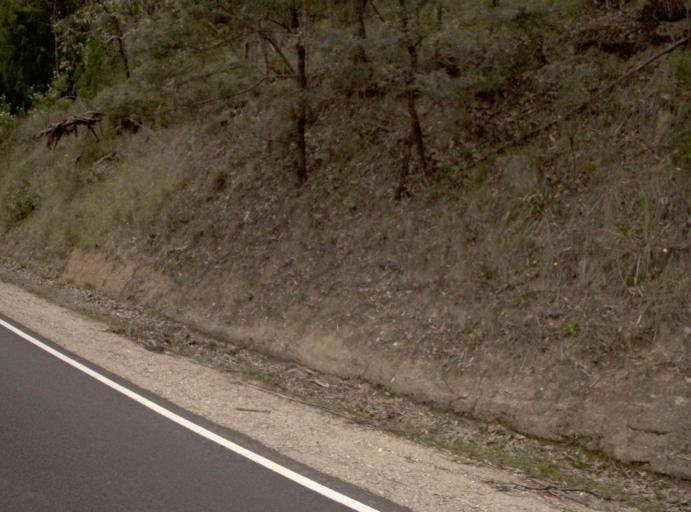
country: AU
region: New South Wales
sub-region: Bombala
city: Bombala
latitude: -37.4599
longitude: 149.1878
